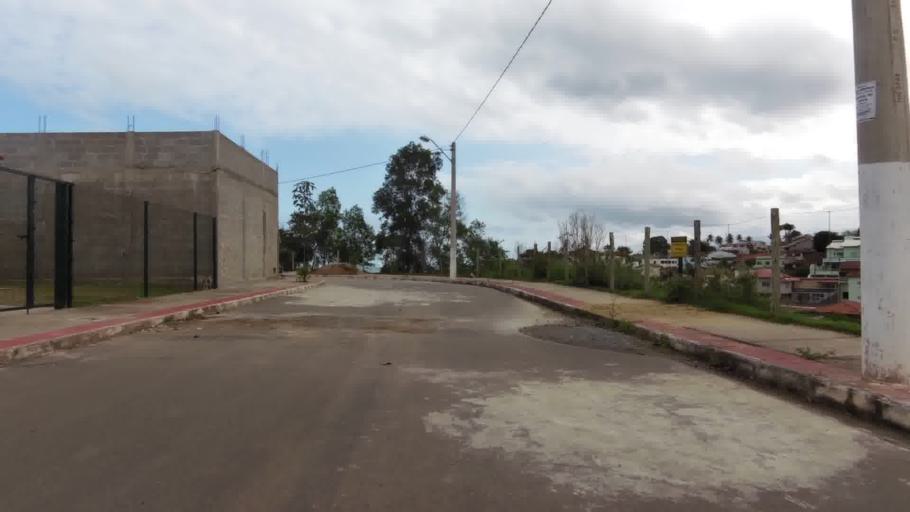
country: BR
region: Espirito Santo
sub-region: Piuma
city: Piuma
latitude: -20.8026
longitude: -40.6485
